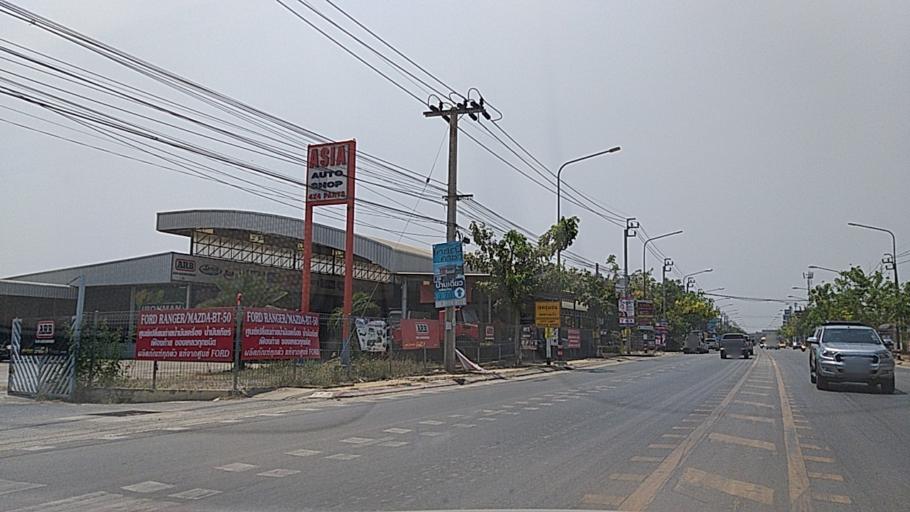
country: TH
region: Nonthaburi
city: Bang Bua Thong
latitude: 13.9083
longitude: 100.3949
